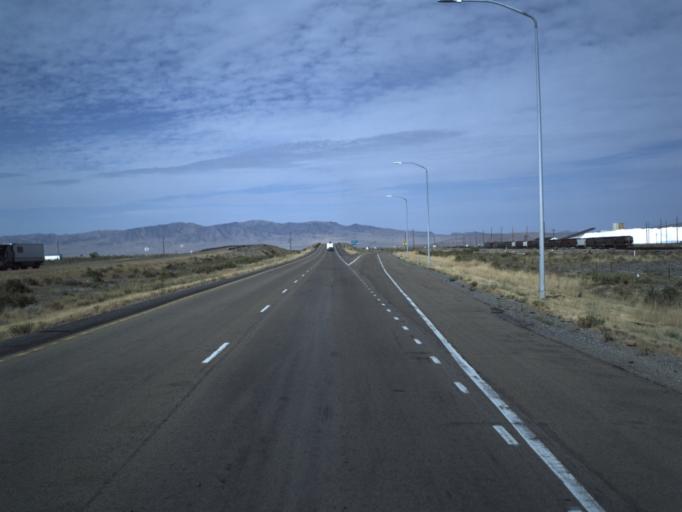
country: US
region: Utah
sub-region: Tooele County
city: Grantsville
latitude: 40.7453
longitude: -112.6451
